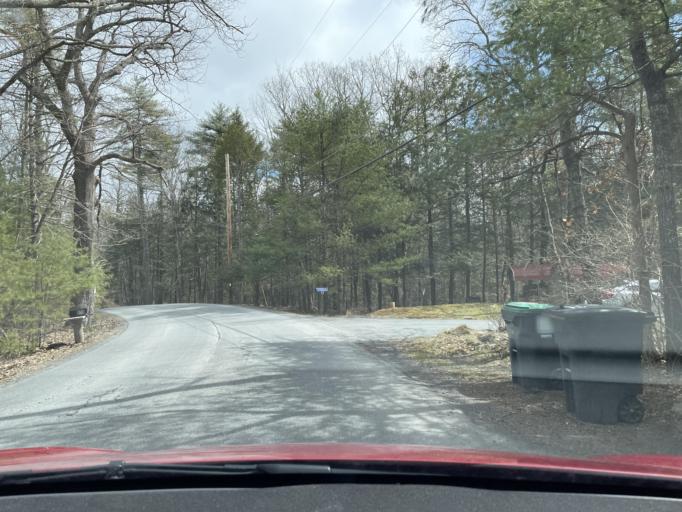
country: US
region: New York
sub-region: Ulster County
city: Zena
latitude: 42.0305
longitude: -74.0422
